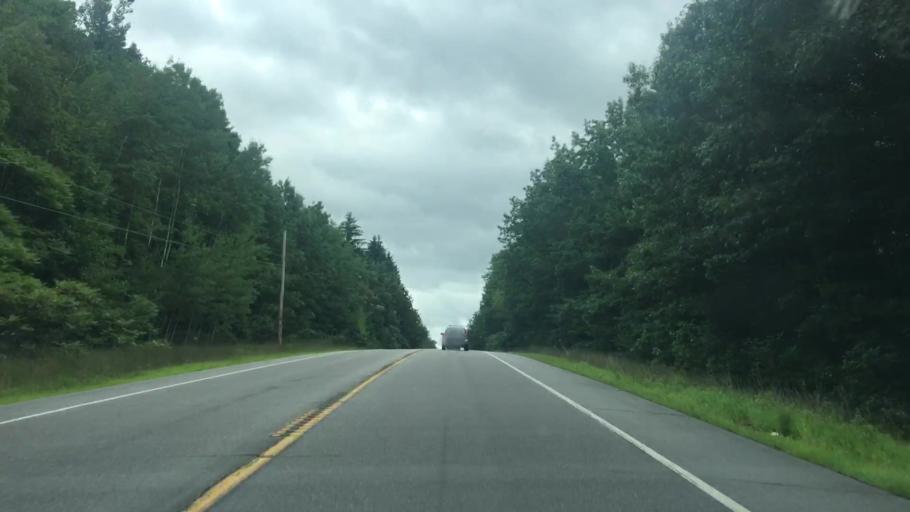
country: US
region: Maine
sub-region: York County
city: Alfred
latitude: 43.5033
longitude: -70.7176
